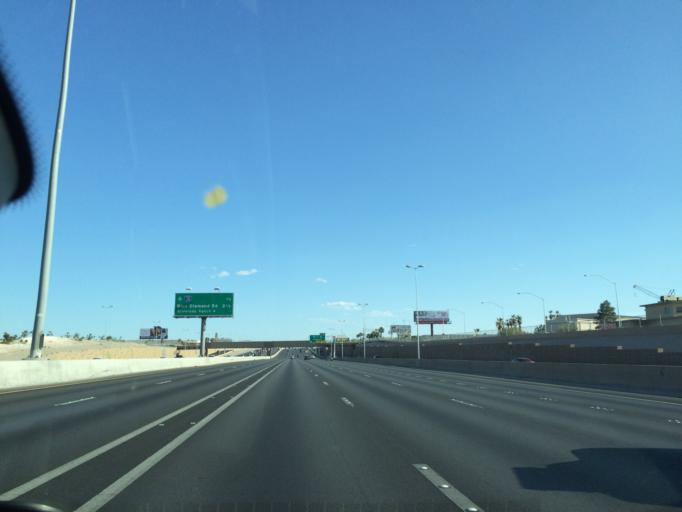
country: US
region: Nevada
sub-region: Clark County
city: Paradise
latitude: 36.0796
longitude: -115.1809
